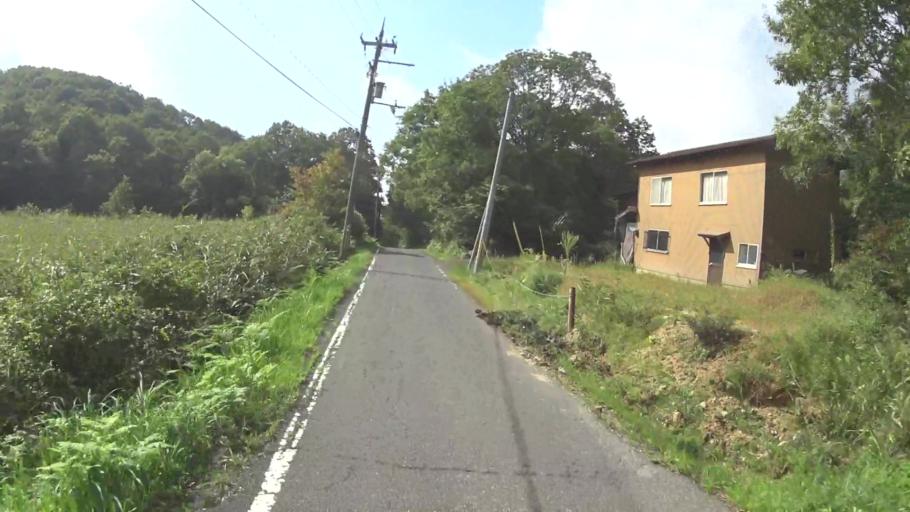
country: JP
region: Kyoto
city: Miyazu
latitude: 35.6514
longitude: 135.1808
